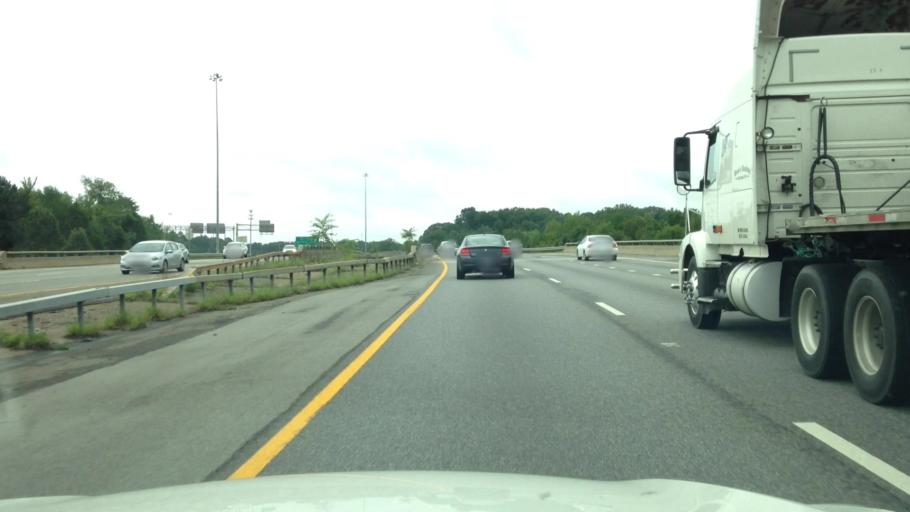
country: US
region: Virginia
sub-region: City of Petersburg
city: Petersburg
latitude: 37.2285
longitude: -77.3957
